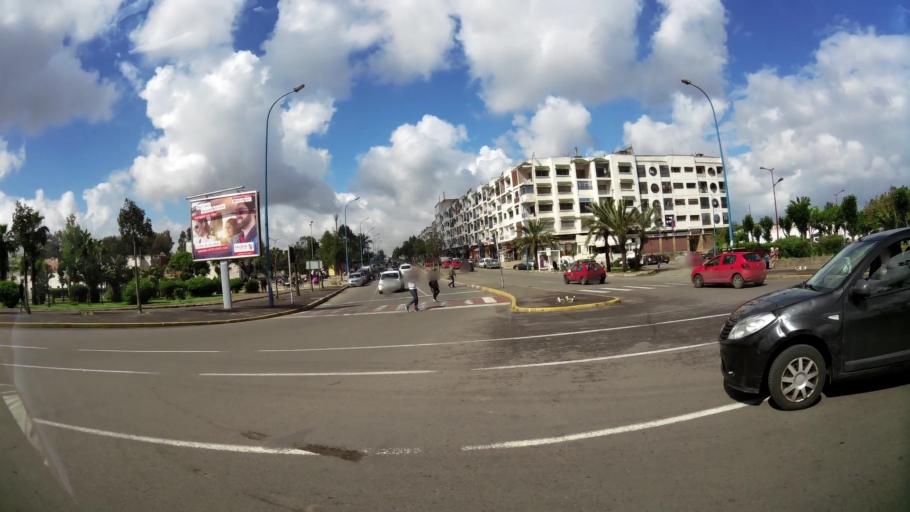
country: MA
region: Grand Casablanca
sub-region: Casablanca
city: Casablanca
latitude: 33.5573
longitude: -7.5941
